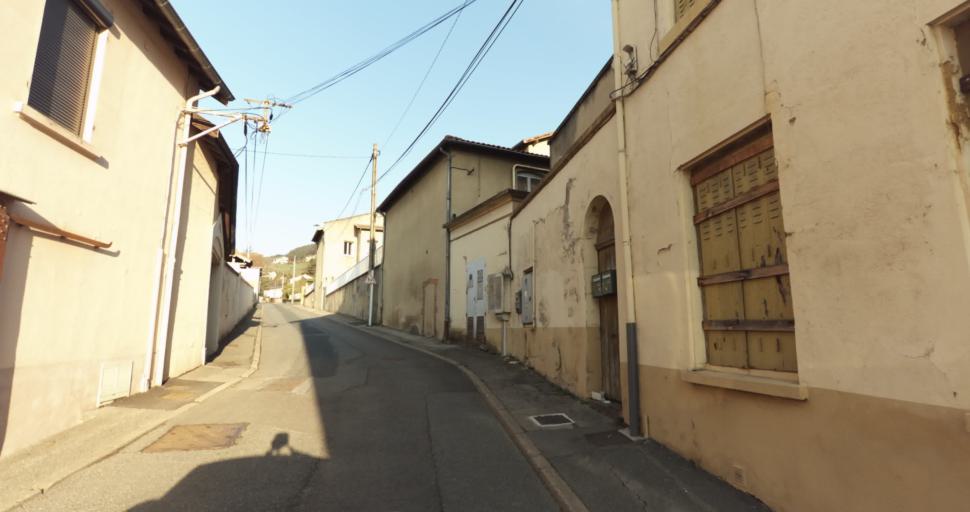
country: FR
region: Rhone-Alpes
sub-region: Departement du Rhone
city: Tarare
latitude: 45.8973
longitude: 4.4286
